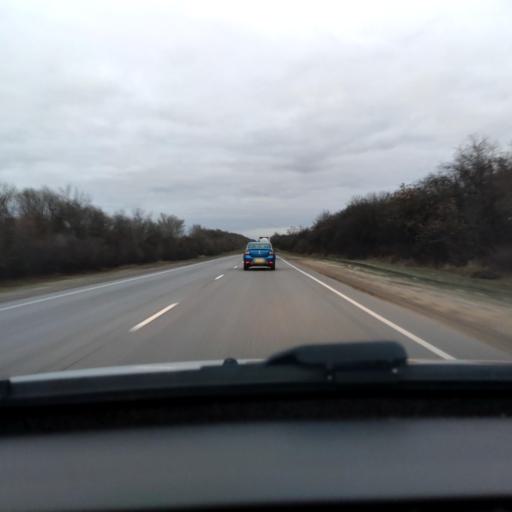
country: RU
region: Lipetsk
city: Borinskoye
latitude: 52.4351
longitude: 39.2726
